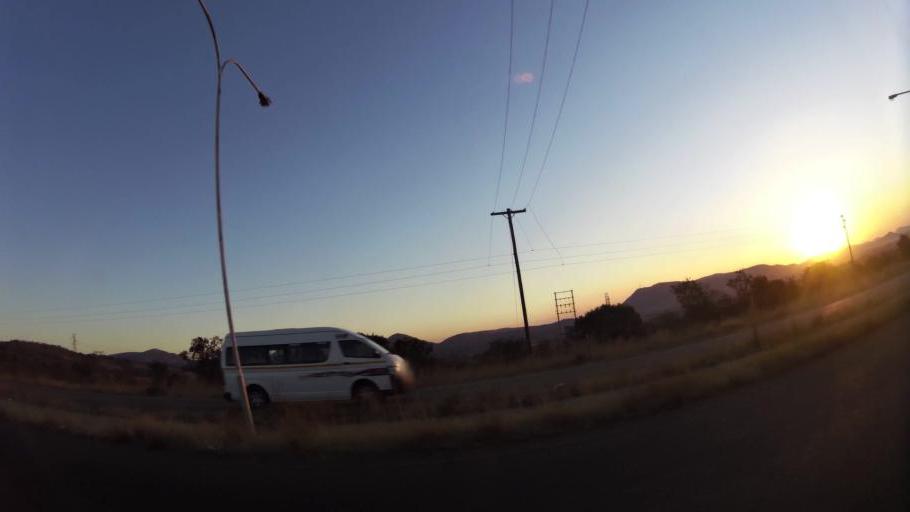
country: ZA
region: North-West
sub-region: Bojanala Platinum District Municipality
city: Rustenburg
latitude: -25.6174
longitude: 27.1801
